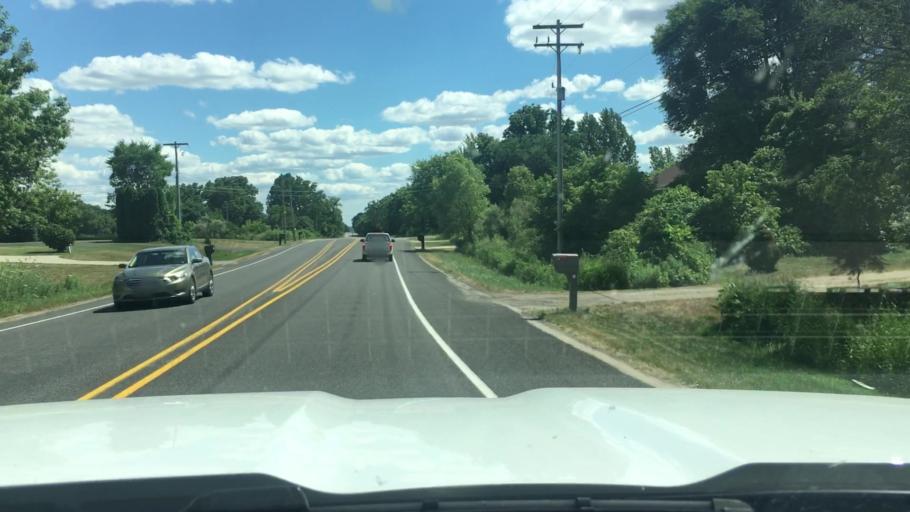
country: US
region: Michigan
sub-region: Kent County
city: Comstock Park
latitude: 43.0735
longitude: -85.6541
